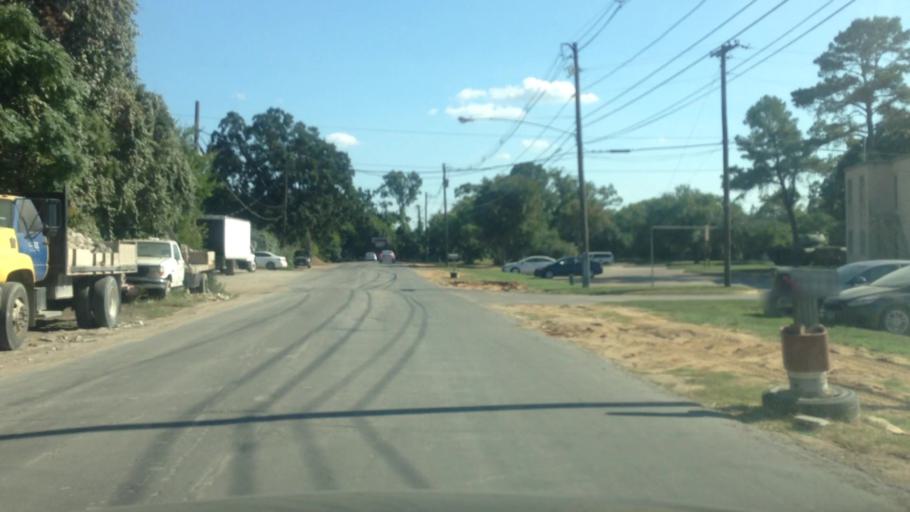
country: US
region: Texas
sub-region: Dallas County
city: Irving
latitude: 32.8684
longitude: -96.9199
